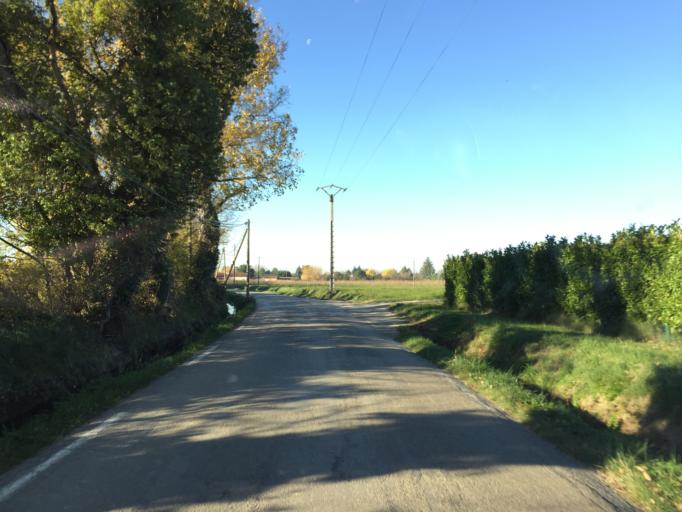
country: FR
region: Provence-Alpes-Cote d'Azur
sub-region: Departement du Vaucluse
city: Sarrians
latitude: 44.0784
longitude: 4.9592
